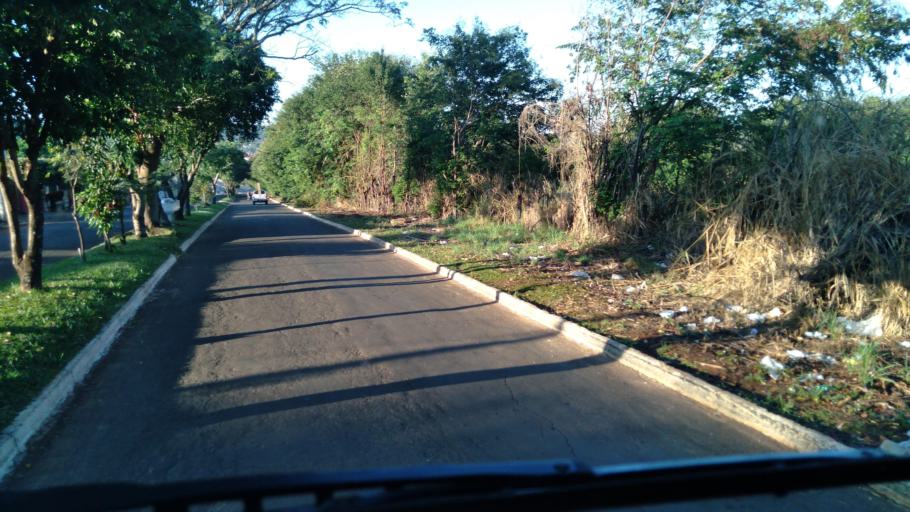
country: BR
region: Goias
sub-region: Mineiros
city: Mineiros
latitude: -17.5752
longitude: -52.5670
